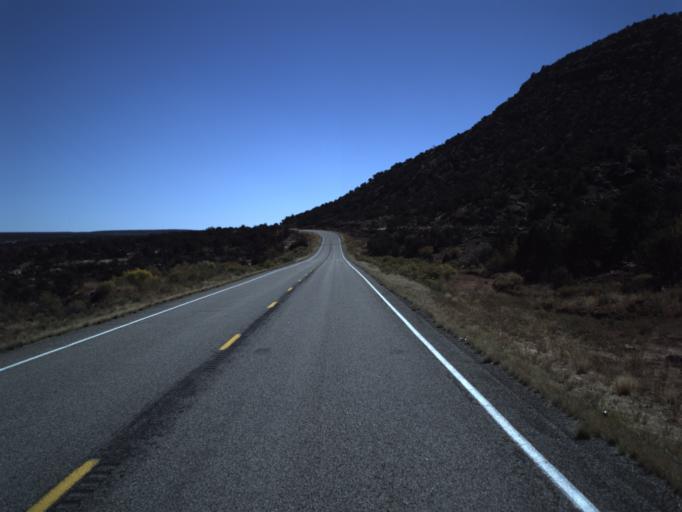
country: US
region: Utah
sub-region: San Juan County
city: Blanding
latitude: 37.6011
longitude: -110.0580
